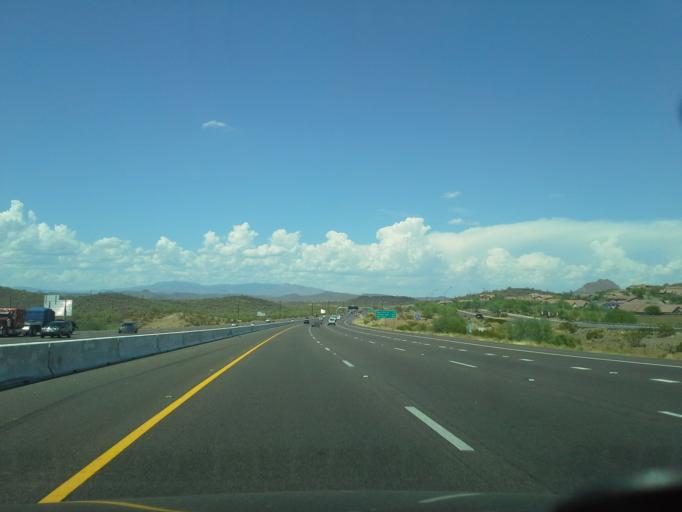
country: US
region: Arizona
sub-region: Maricopa County
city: Anthem
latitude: 33.8257
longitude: -112.1434
